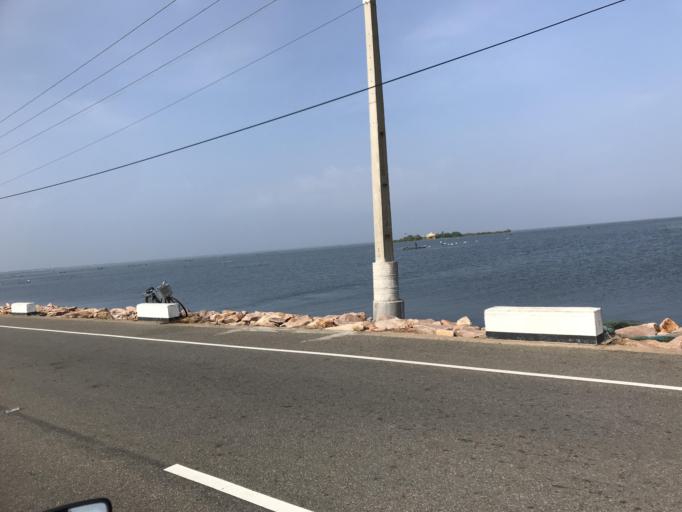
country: LK
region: Northern Province
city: Jaffna
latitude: 9.6531
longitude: 79.9986
